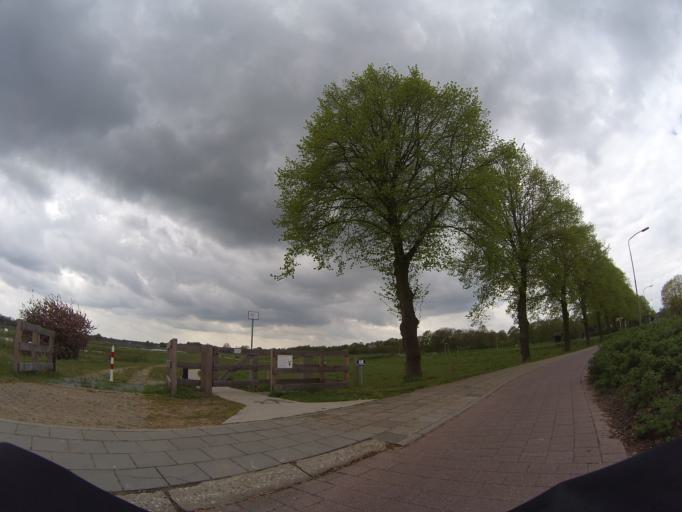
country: NL
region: Overijssel
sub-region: Gemeente Hardenberg
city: Hardenberg
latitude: 52.5726
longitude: 6.6134
